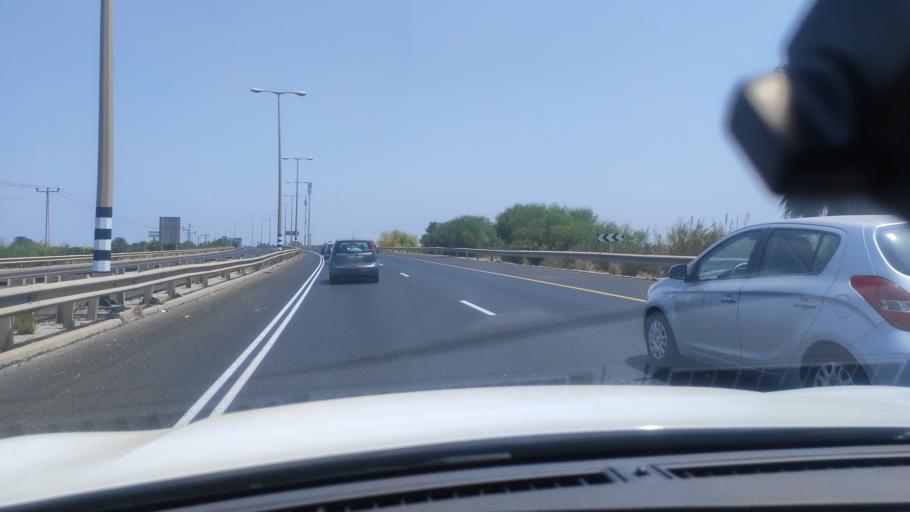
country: IL
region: Central District
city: Petah Tiqwa
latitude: 32.1084
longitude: 34.9015
